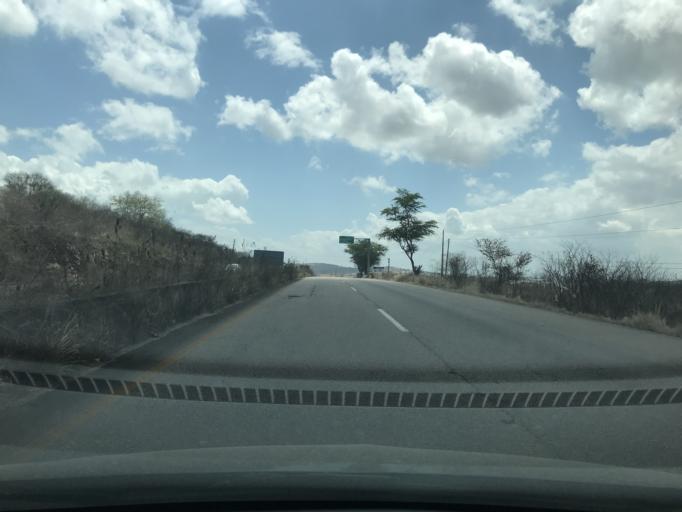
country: BR
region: Pernambuco
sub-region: Caruaru
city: Caruaru
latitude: -8.3064
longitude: -35.9381
